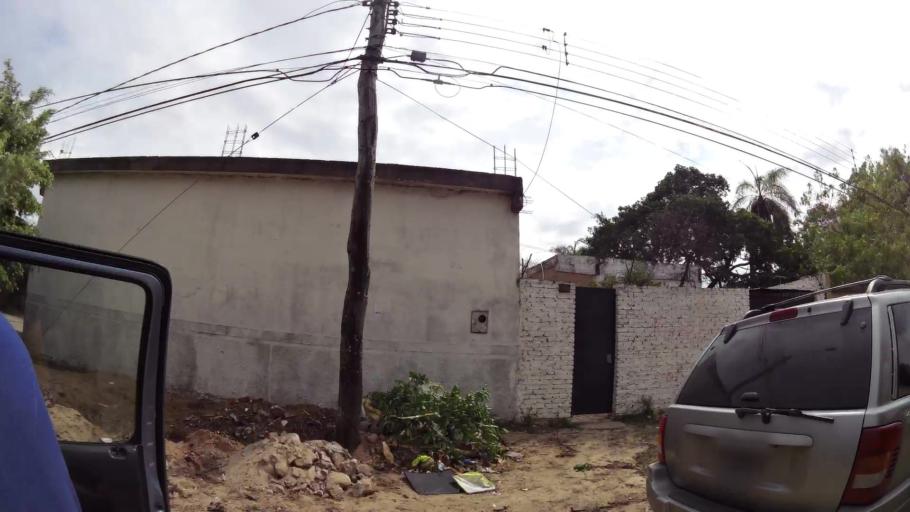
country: BO
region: Santa Cruz
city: Santa Cruz de la Sierra
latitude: -17.7739
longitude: -63.2103
